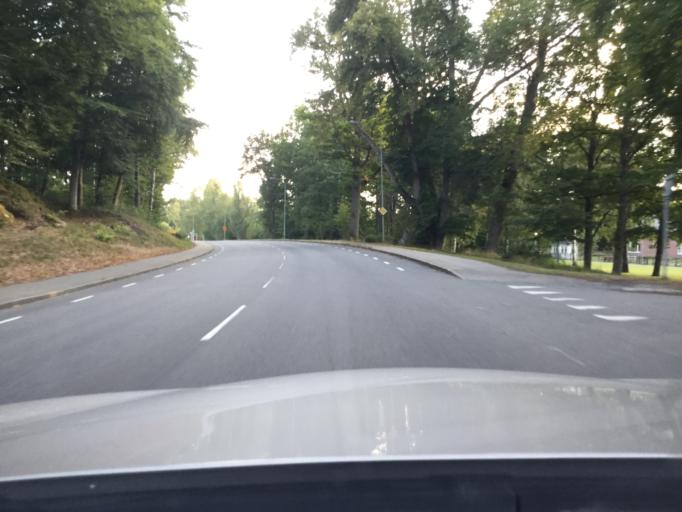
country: SE
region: Kronoberg
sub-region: Almhults Kommun
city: AElmhult
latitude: 56.6431
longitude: 14.2230
